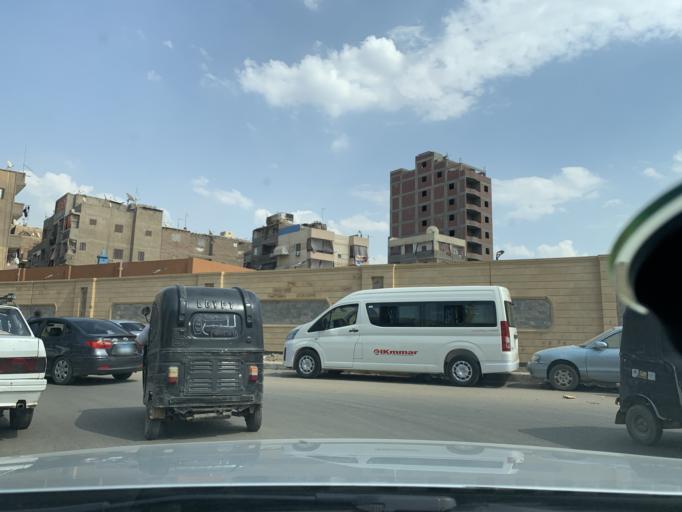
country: EG
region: Muhafazat al Qahirah
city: Cairo
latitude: 30.1138
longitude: 31.3016
